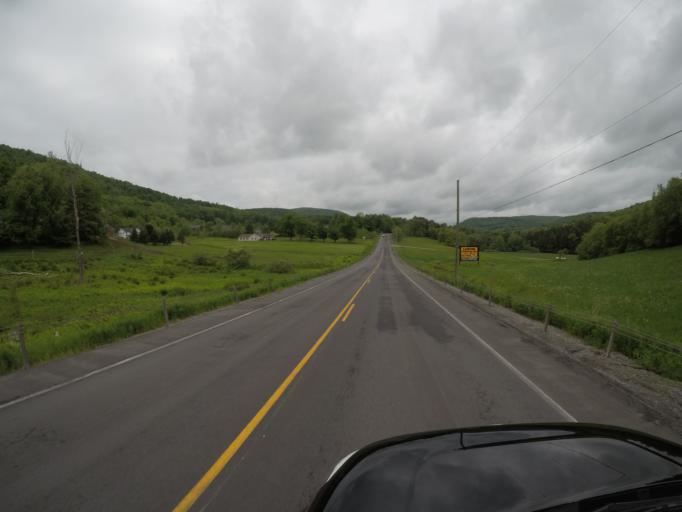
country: US
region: New York
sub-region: Delaware County
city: Delhi
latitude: 42.2448
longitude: -74.8091
